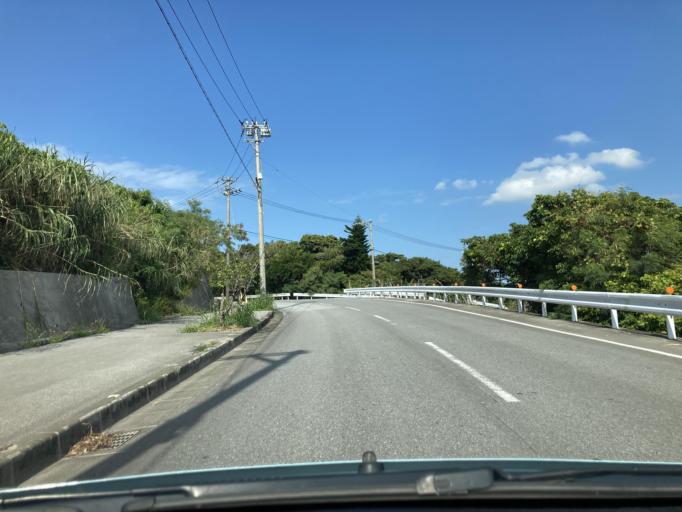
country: JP
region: Okinawa
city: Ginowan
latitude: 26.2790
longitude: 127.7988
